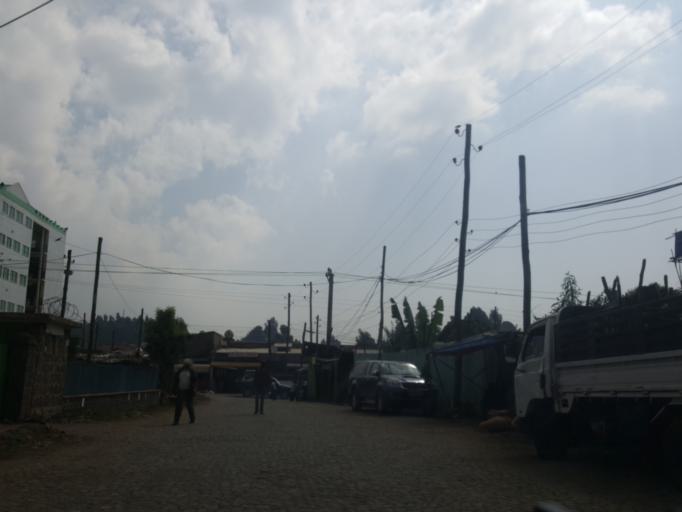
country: ET
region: Adis Abeba
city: Addis Ababa
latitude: 9.0625
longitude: 38.7193
